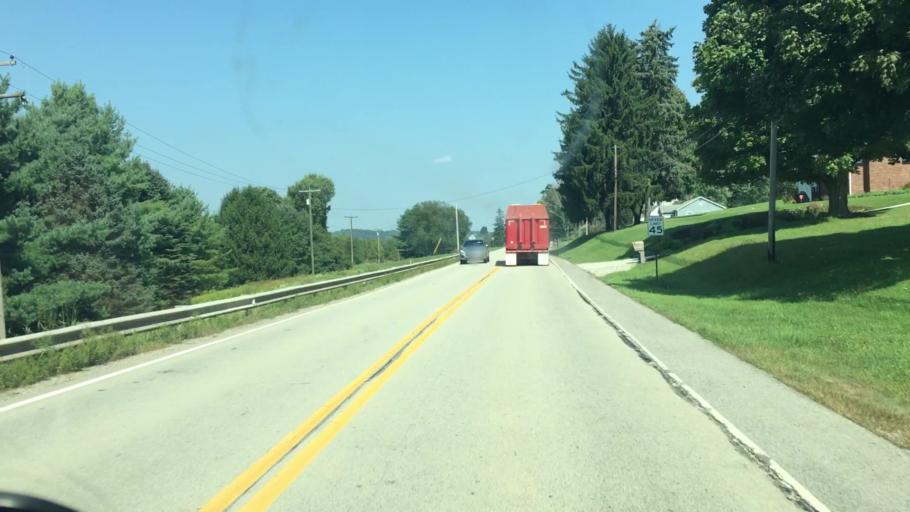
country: US
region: Pennsylvania
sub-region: Washington County
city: Washington
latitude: 40.1112
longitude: -80.2936
